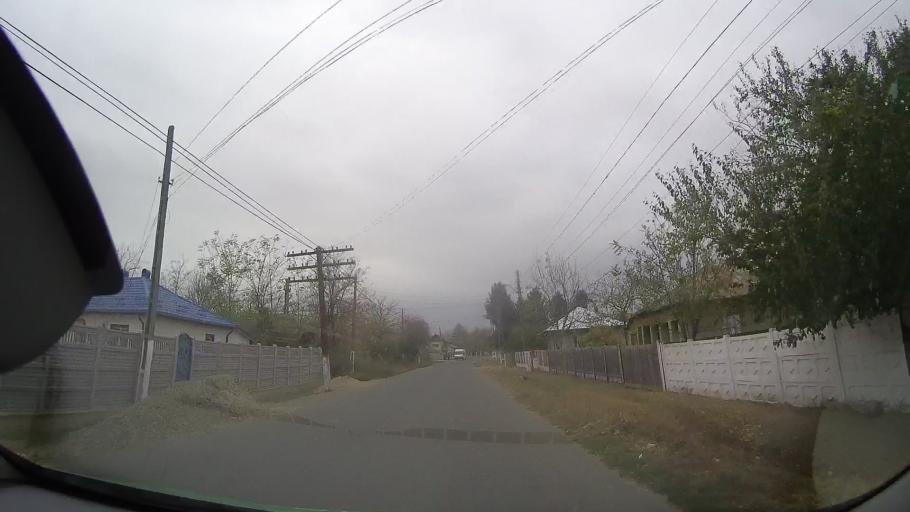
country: RO
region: Braila
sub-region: Comuna Ulmu
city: Jugureanu
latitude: 44.9424
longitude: 27.2796
